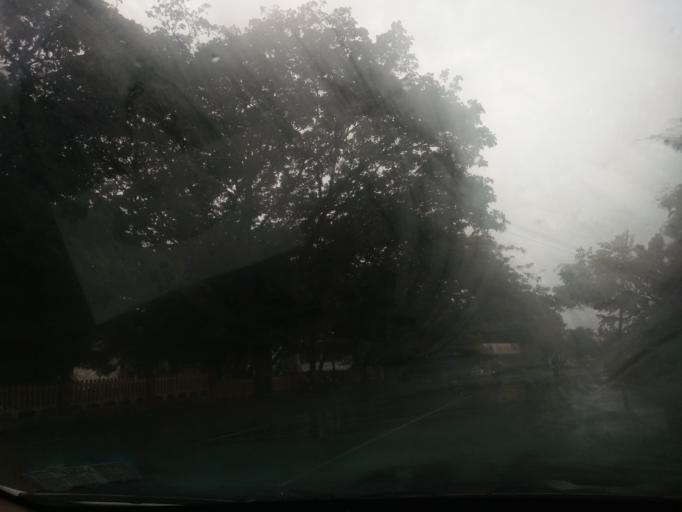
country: IN
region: Goa
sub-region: North Goa
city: Panaji
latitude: 15.5183
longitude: 73.8293
